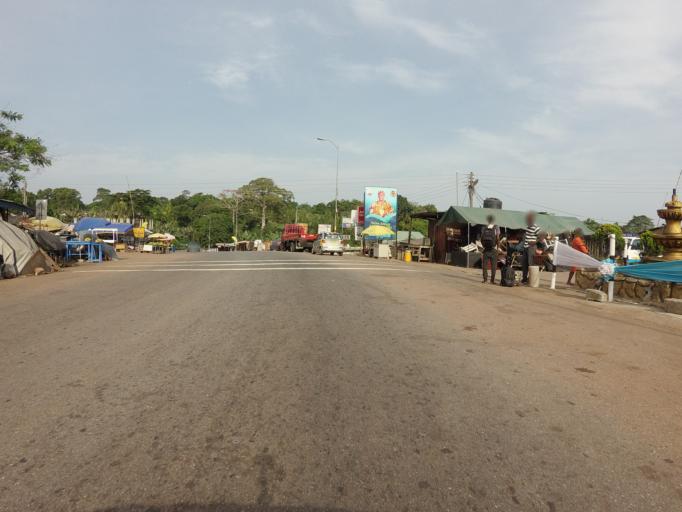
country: GH
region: Eastern
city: Aburi
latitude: 5.8139
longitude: -0.1866
